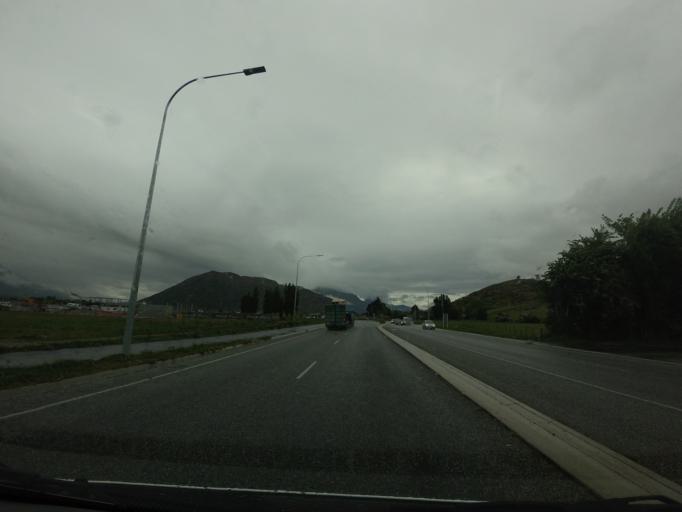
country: NZ
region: Otago
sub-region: Queenstown-Lakes District
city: Queenstown
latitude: -45.0080
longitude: 168.7464
